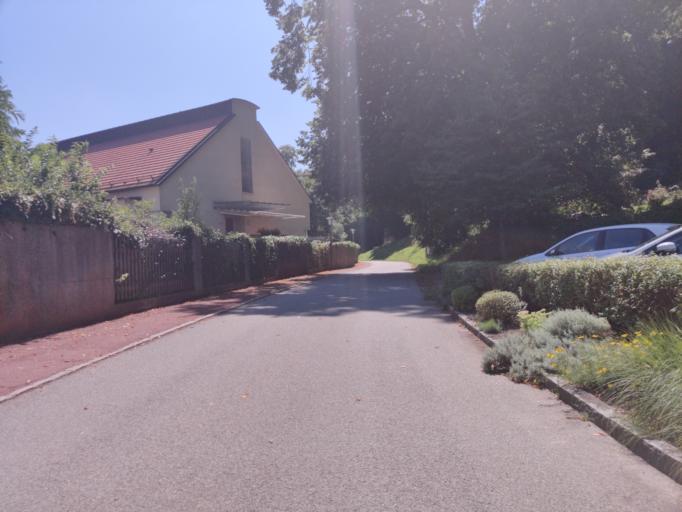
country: AT
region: Upper Austria
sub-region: Politischer Bezirk Rohrbach
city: Pfarrkirchen im Muehlkreis
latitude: 48.4996
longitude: 13.7332
